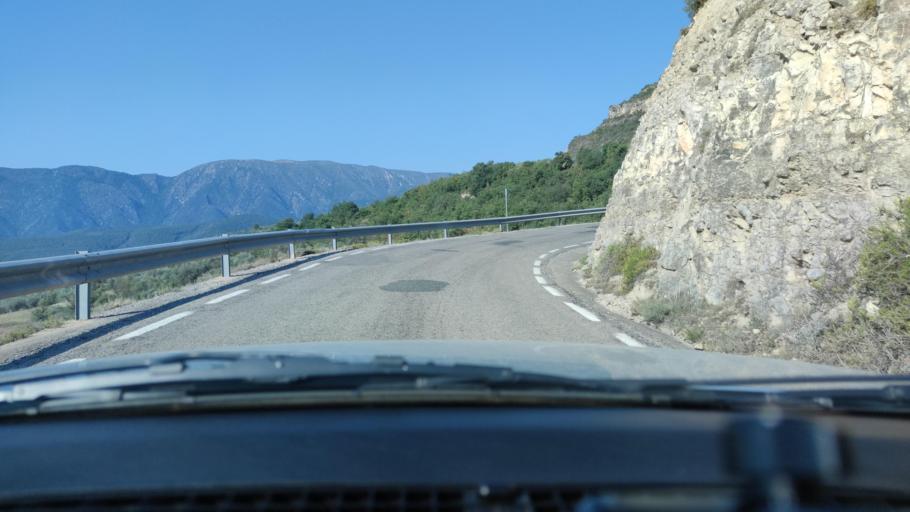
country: ES
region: Catalonia
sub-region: Provincia de Lleida
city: Llimiana
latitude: 42.0877
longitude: 0.8720
